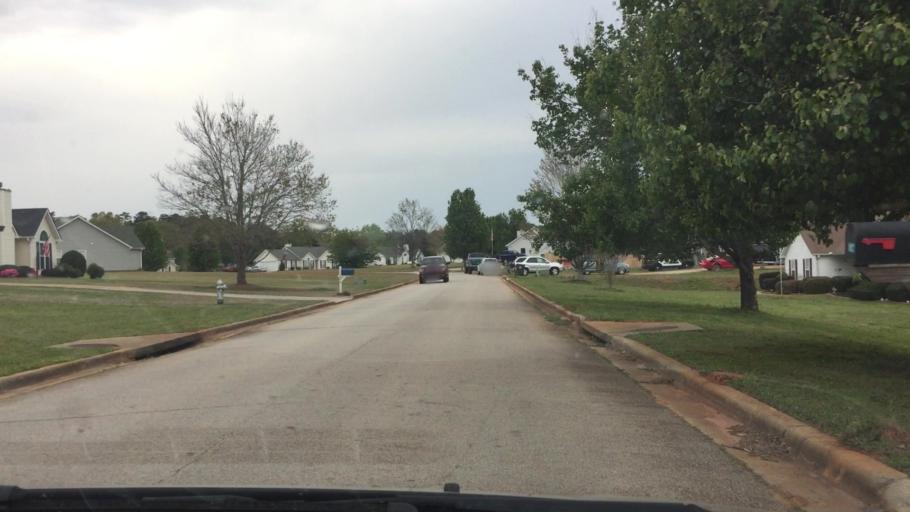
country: US
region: Georgia
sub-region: Henry County
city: Locust Grove
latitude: 33.3340
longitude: -84.0963
